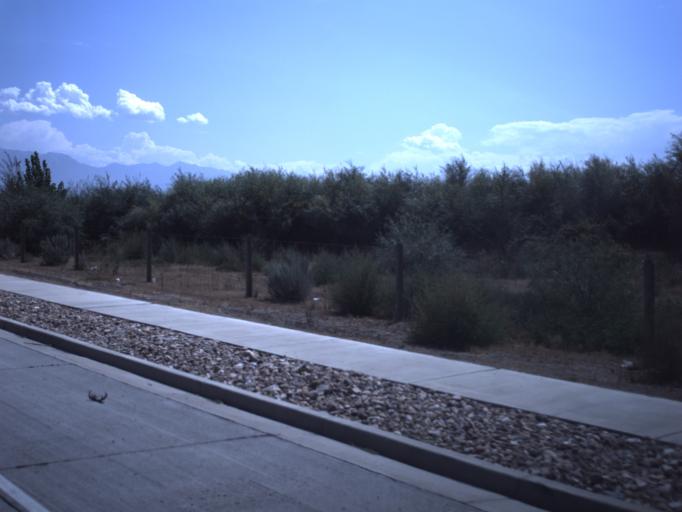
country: US
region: Utah
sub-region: Utah County
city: Lehi
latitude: 40.3760
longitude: -111.8742
